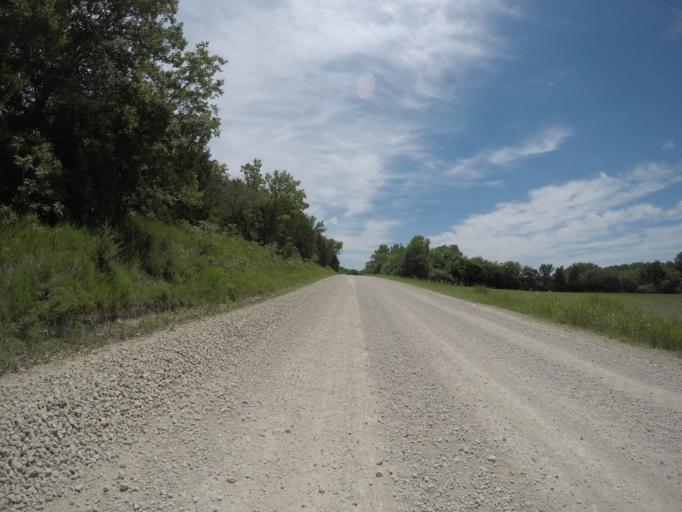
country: US
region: Kansas
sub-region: Wabaunsee County
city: Alma
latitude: 38.9759
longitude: -96.2644
